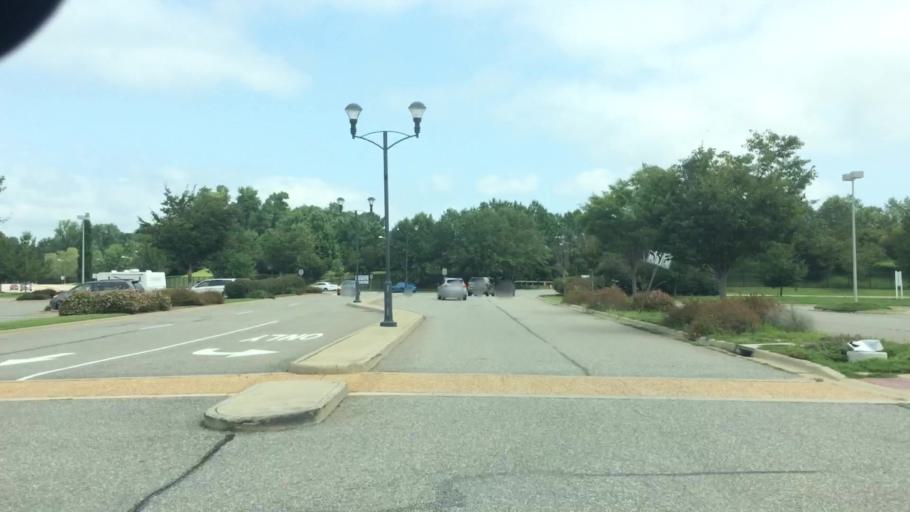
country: US
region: Virginia
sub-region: City of Williamsburg
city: Williamsburg
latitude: 37.2584
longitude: -76.6400
